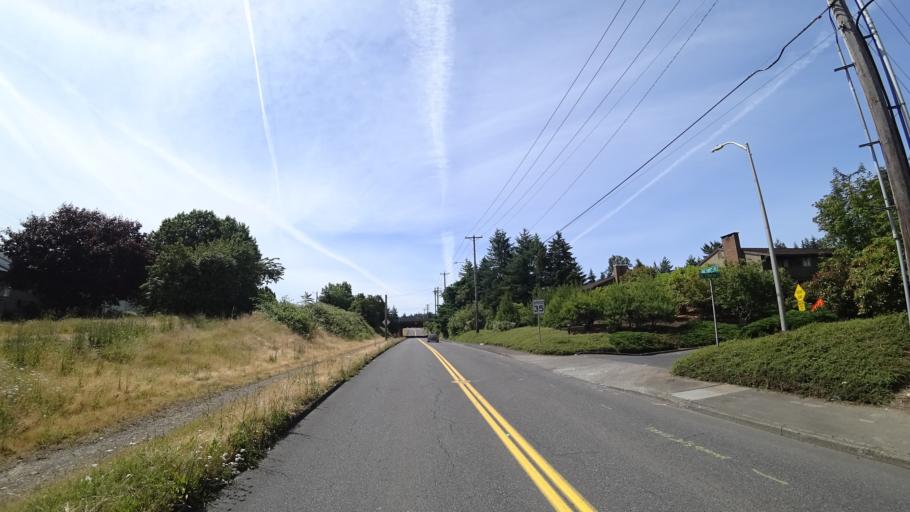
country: US
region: Oregon
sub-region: Multnomah County
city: Fairview
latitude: 45.5445
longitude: -122.5103
